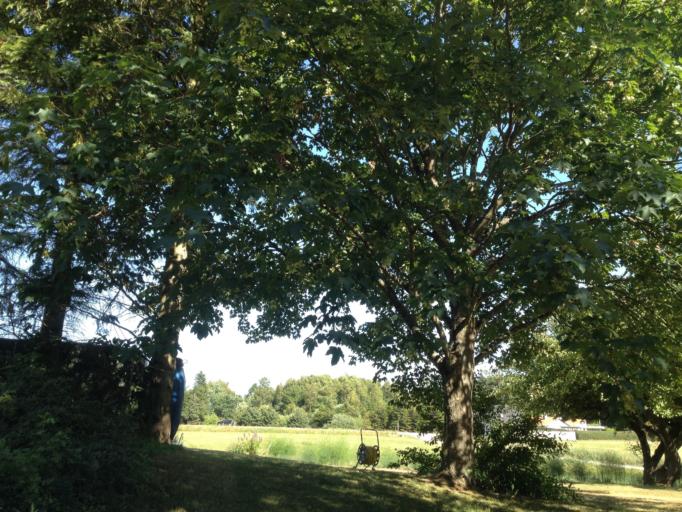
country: DK
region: Capital Region
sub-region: Gribskov Kommune
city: Graested
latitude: 56.0583
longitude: 12.3391
